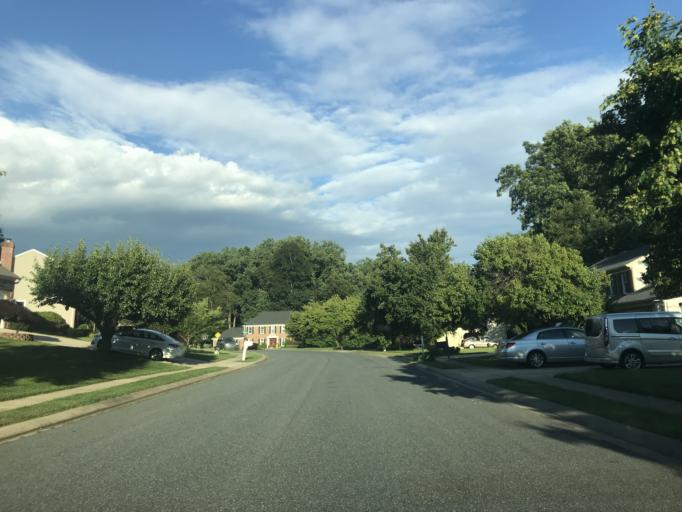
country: US
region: Maryland
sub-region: Harford County
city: South Bel Air
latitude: 39.5614
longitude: -76.3158
